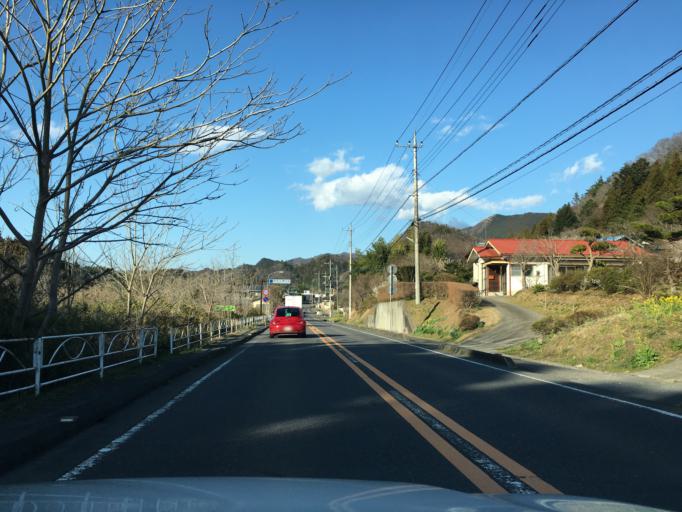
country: JP
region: Ibaraki
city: Daigo
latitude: 36.7071
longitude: 140.3833
